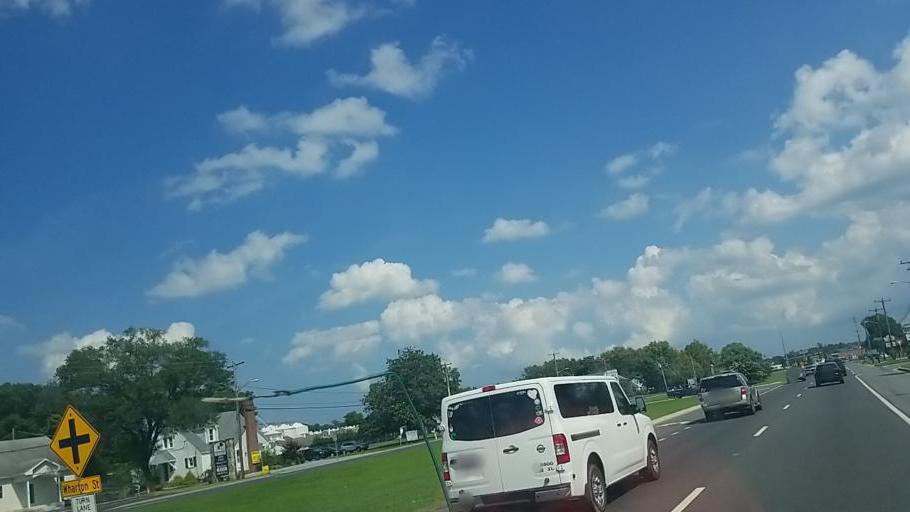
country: US
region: Delaware
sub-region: Sussex County
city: Millsboro
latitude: 38.5882
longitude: -75.3001
